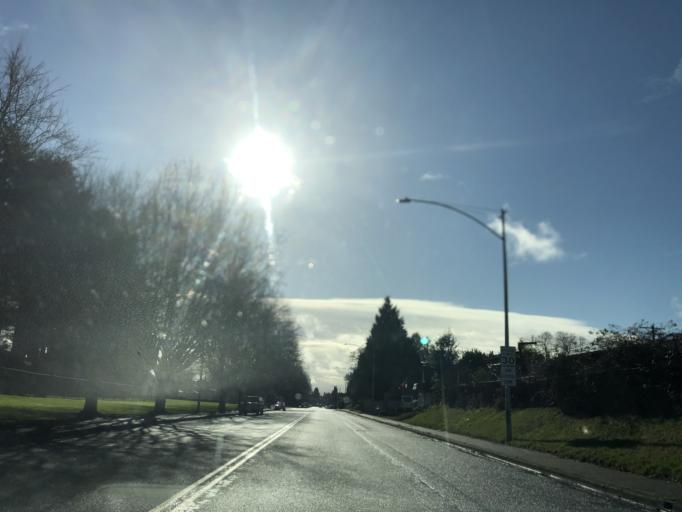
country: US
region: Washington
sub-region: Pierce County
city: Tacoma
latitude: 47.2420
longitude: -122.4591
